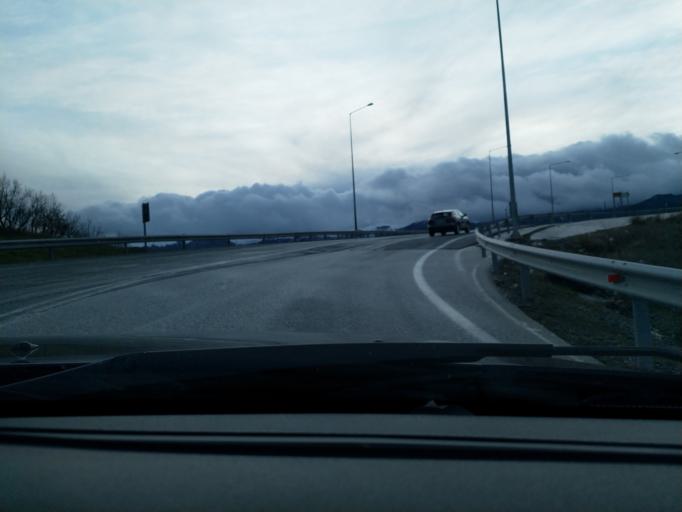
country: GR
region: Epirus
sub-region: Nomos Ioanninon
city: Metsovo
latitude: 39.7921
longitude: 21.3181
